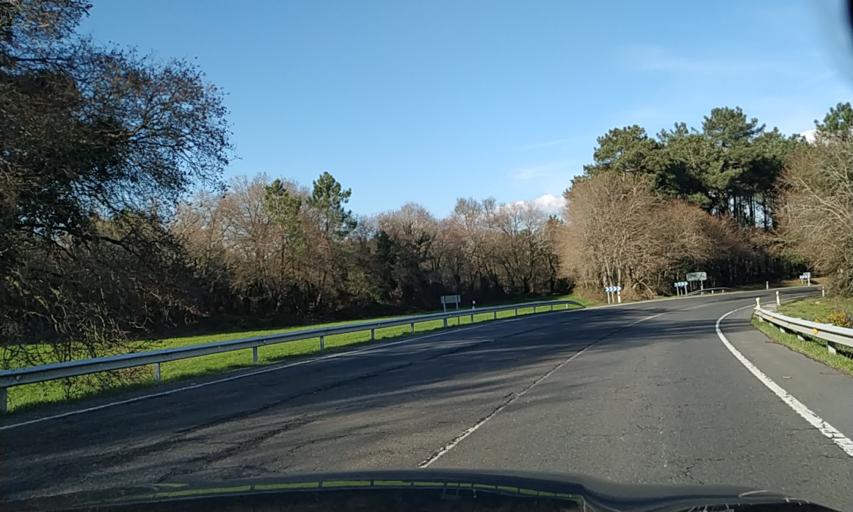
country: ES
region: Galicia
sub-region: Provincia de Pontevedra
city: Silleda
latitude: 42.7038
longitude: -8.3105
